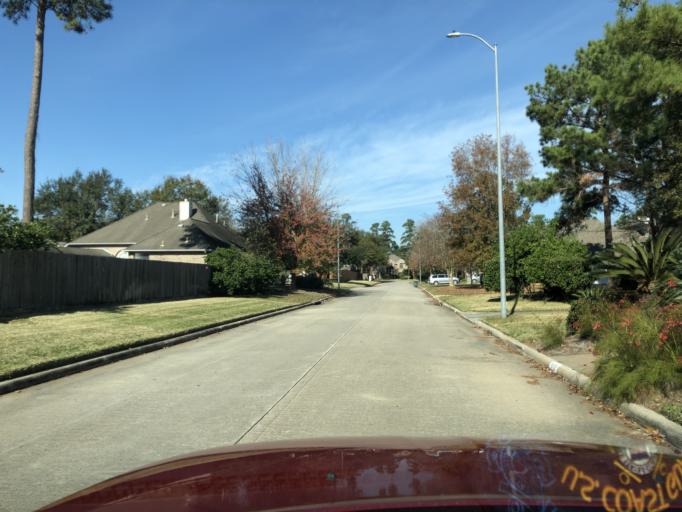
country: US
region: Texas
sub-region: Harris County
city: Tomball
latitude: 30.0223
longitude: -95.5557
